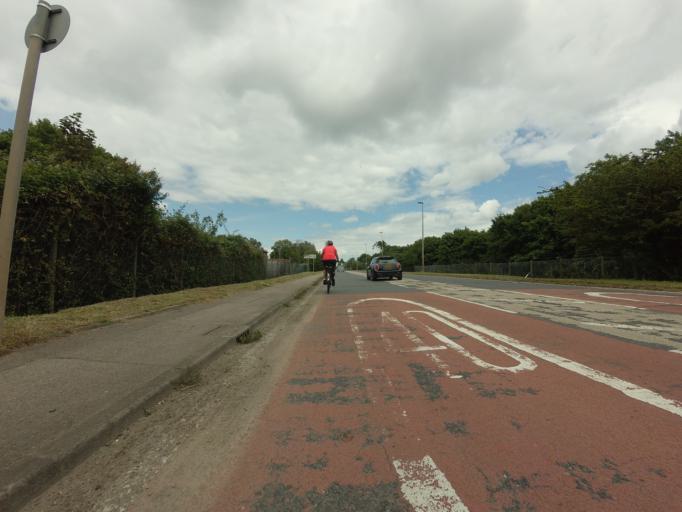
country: GB
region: England
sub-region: Medway
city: Allhallows
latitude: 51.4444
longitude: 0.6906
